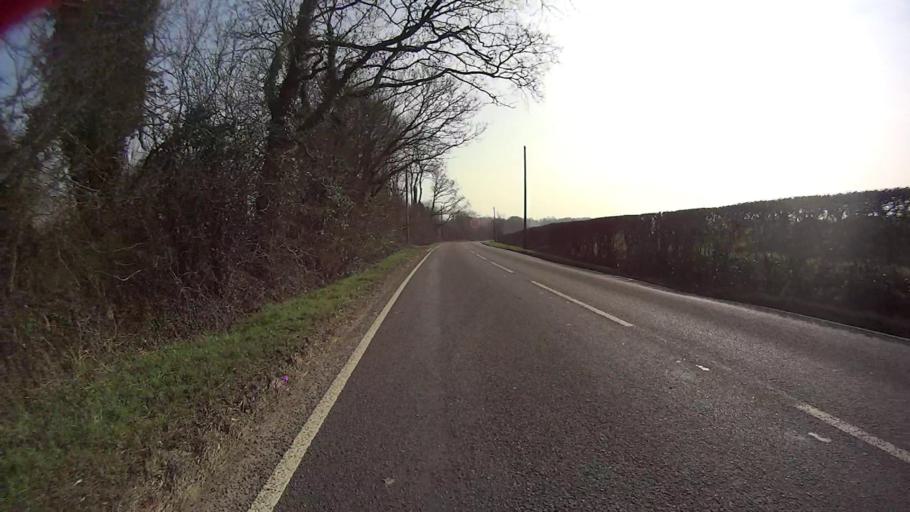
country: GB
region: England
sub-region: Surrey
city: Salfords
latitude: 51.2093
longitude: -0.1530
